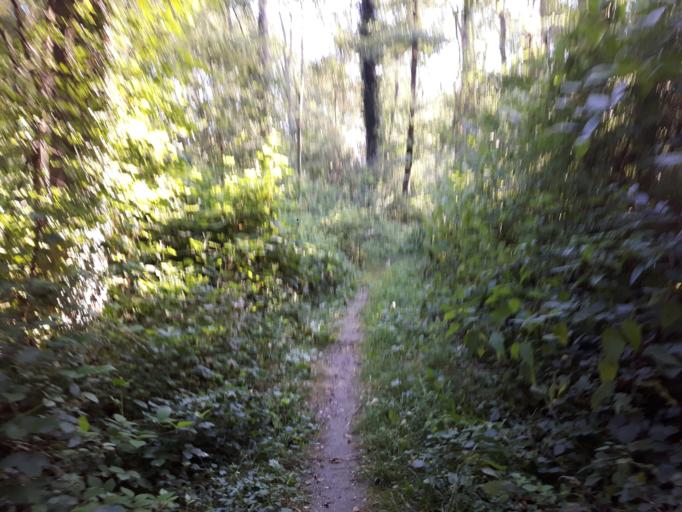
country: DE
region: Baden-Wuerttemberg
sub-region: Karlsruhe Region
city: Karlsdorf-Neuthard
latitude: 49.1013
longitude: 8.5392
